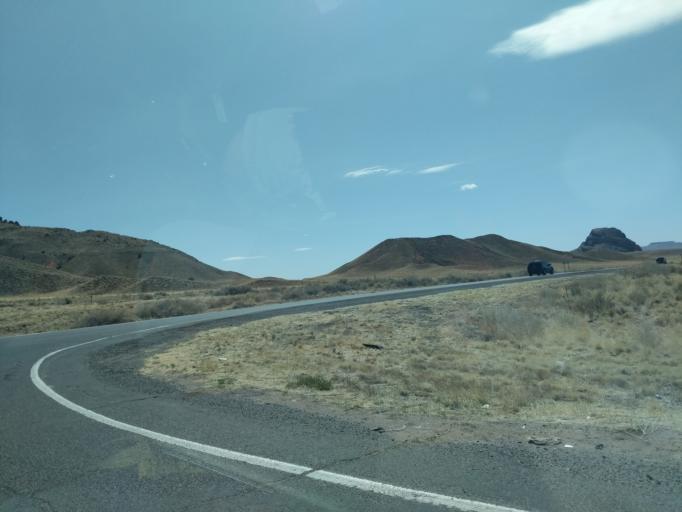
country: US
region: Arizona
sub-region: Navajo County
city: Dilkon
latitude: 35.4005
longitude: -110.0654
